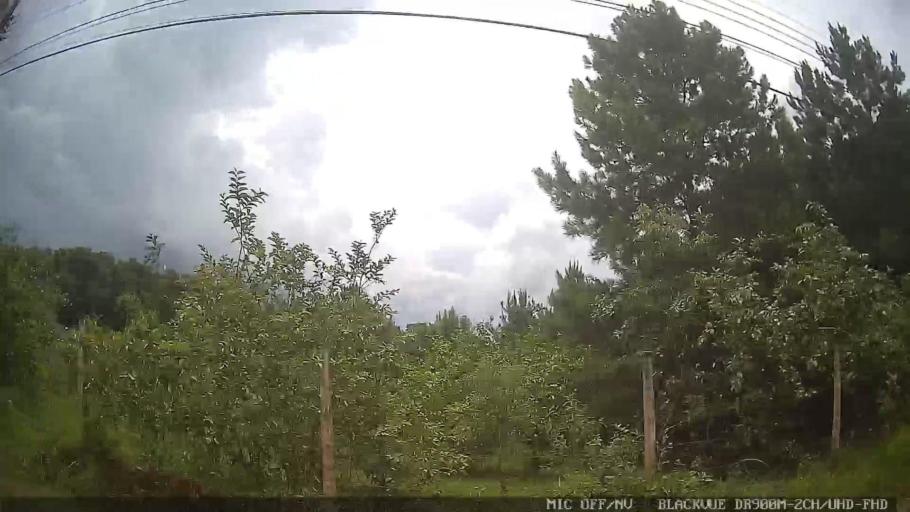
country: BR
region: Sao Paulo
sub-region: Santa Isabel
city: Santa Isabel
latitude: -23.3802
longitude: -46.2338
